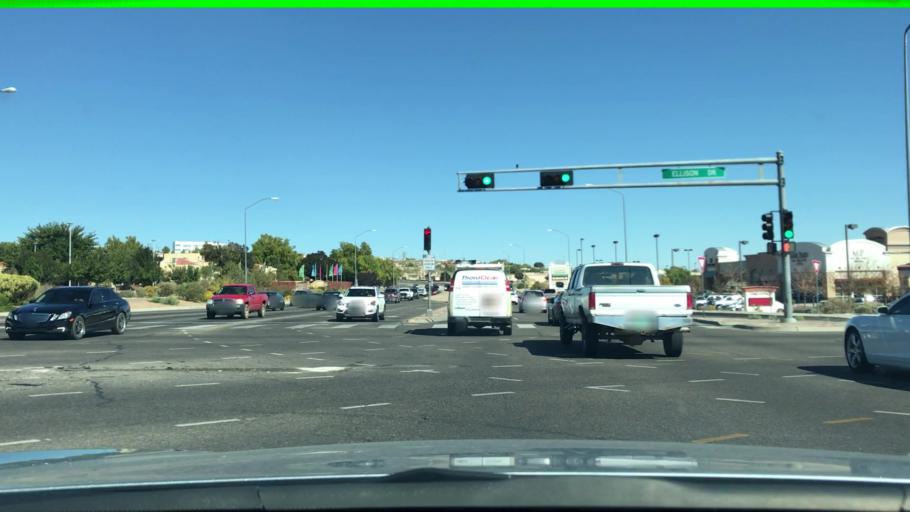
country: US
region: New Mexico
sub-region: Sandoval County
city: Rio Rancho
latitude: 35.2056
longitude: -106.6591
